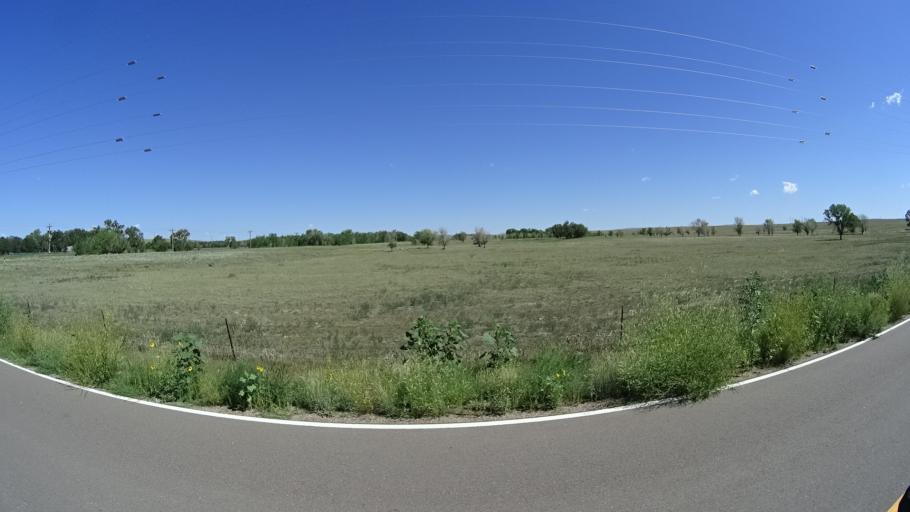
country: US
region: Colorado
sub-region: El Paso County
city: Security-Widefield
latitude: 38.7809
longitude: -104.6490
